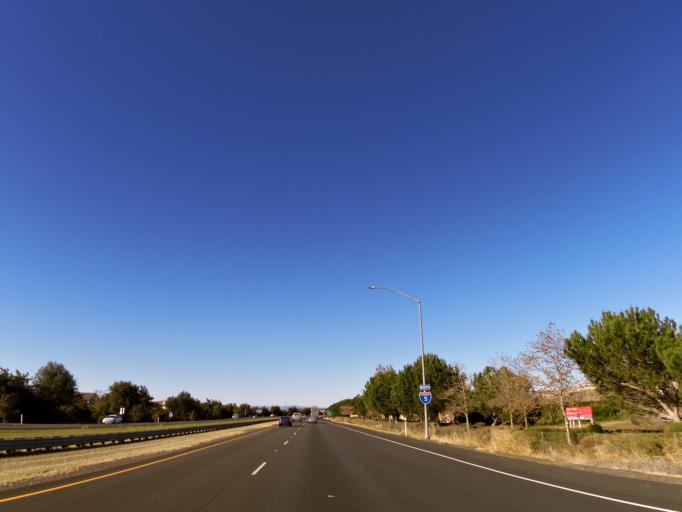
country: US
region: California
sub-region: Yolo County
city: Woodland
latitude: 38.6739
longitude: -121.7339
